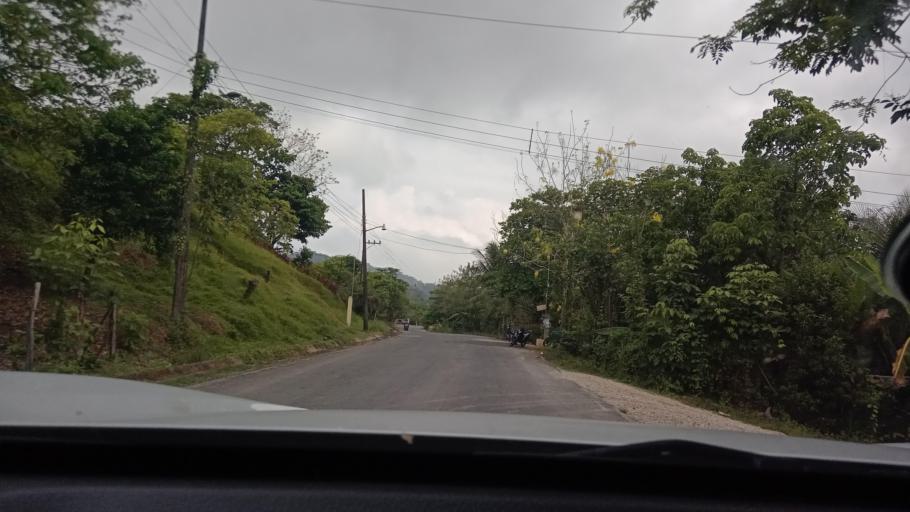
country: MX
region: Tabasco
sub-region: Huimanguillo
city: Francisco Rueda
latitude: 17.5295
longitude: -94.1266
